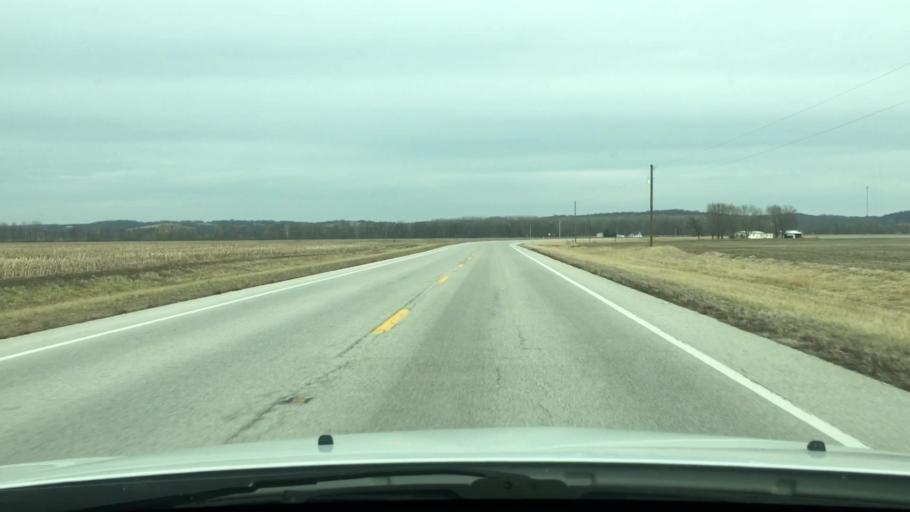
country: US
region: Missouri
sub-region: Pike County
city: Louisiana
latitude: 39.4961
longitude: -91.0045
